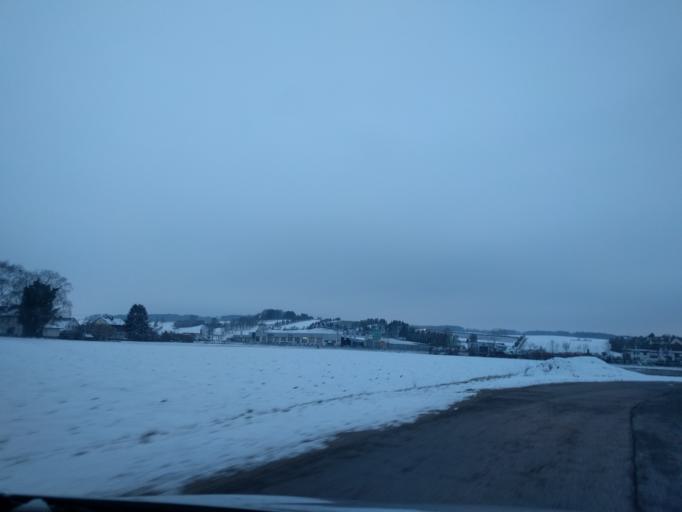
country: DE
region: Bavaria
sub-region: Swabia
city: Donauwoerth
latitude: 48.7061
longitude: 10.7555
